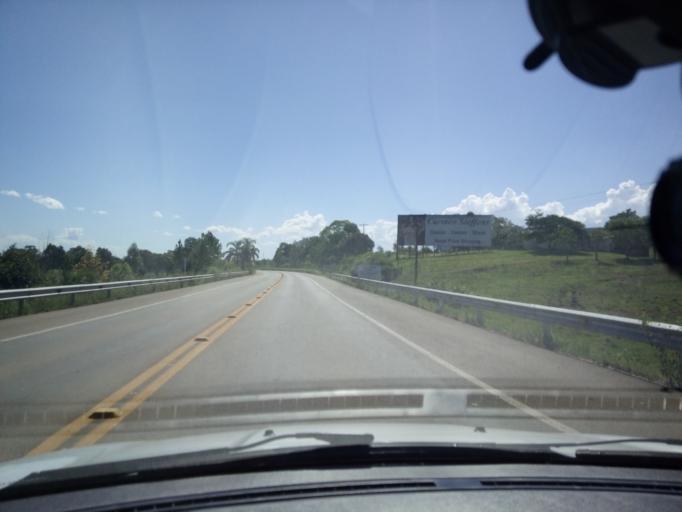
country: BR
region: Rio Grande do Sul
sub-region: Santa Maria
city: Santa Maria
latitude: -29.7325
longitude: -53.5141
